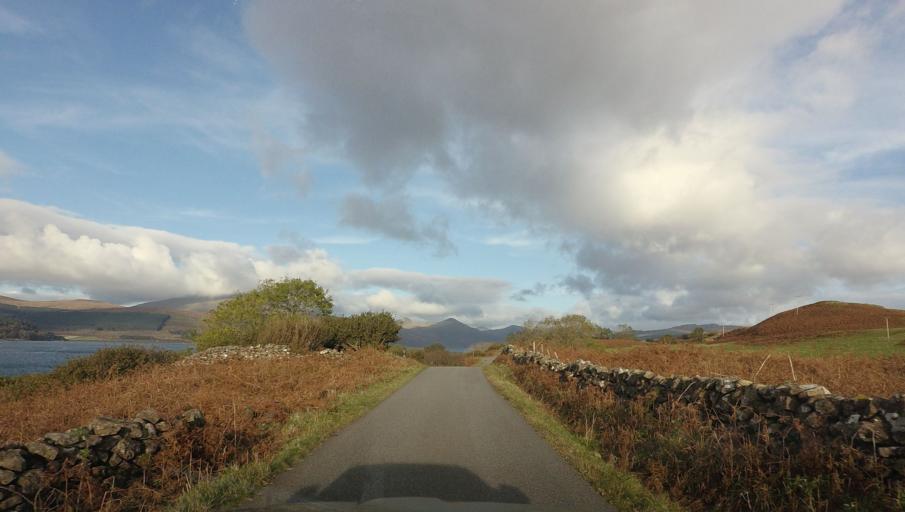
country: GB
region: Scotland
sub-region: Argyll and Bute
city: Isle Of Mull
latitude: 56.3511
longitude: -6.0849
